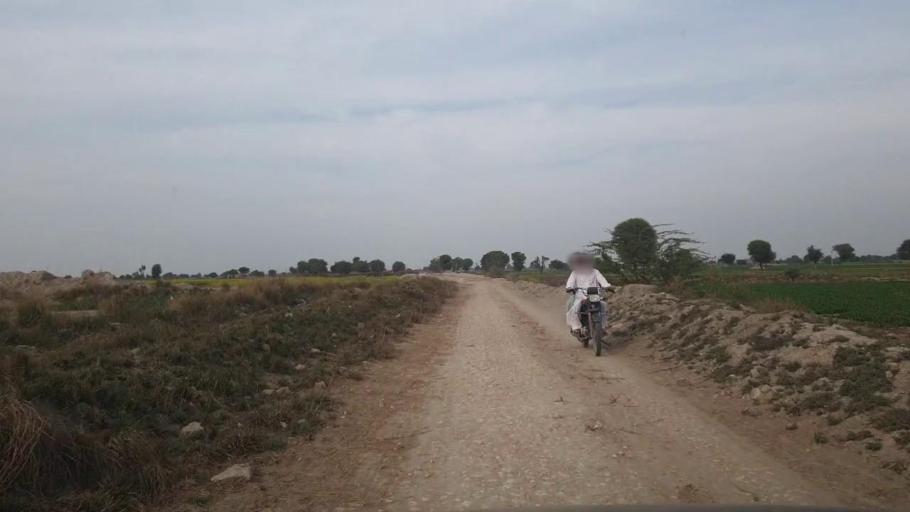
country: PK
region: Sindh
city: Shahpur Chakar
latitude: 26.1191
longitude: 68.5102
